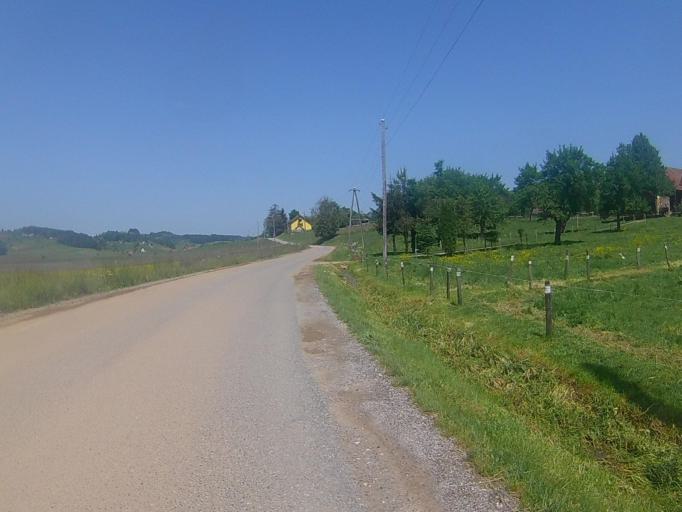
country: SI
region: Sveti Jurij v Slovenskih Goricah
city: Jurovski Dol
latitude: 46.5810
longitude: 15.7527
